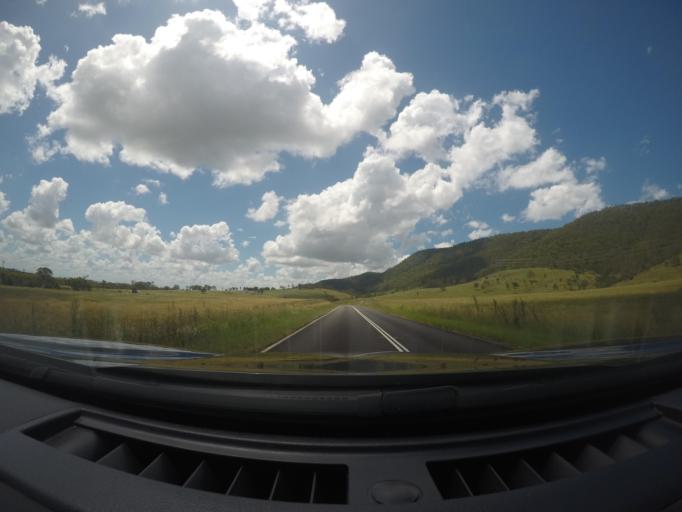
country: AU
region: Queensland
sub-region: Moreton Bay
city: Woodford
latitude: -27.1445
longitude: 152.5245
